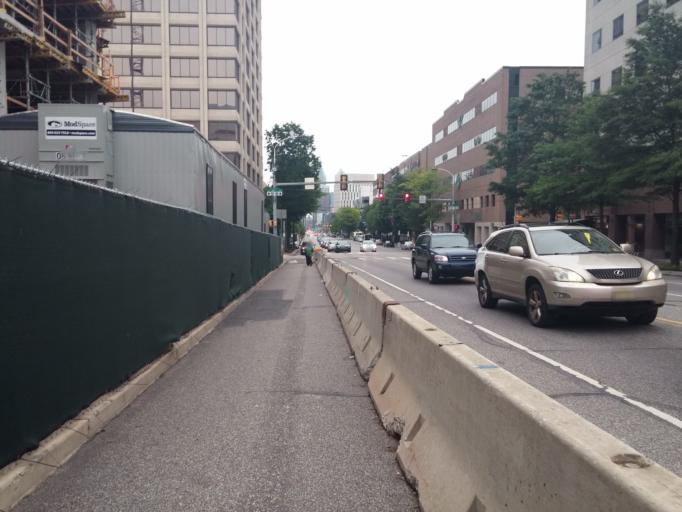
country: US
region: Pennsylvania
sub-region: Philadelphia County
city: Philadelphia
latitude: 39.9563
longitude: -75.1950
